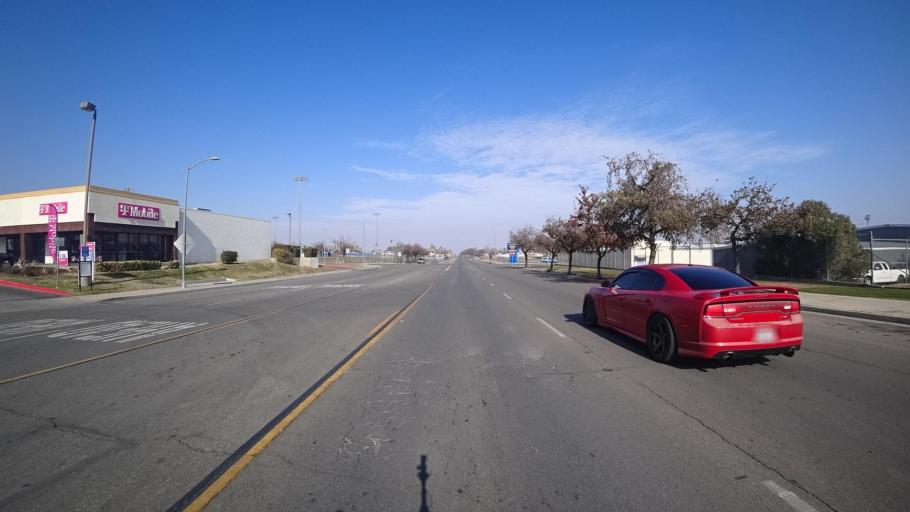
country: US
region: California
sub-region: Kern County
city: Taft
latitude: 35.1459
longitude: -119.4651
